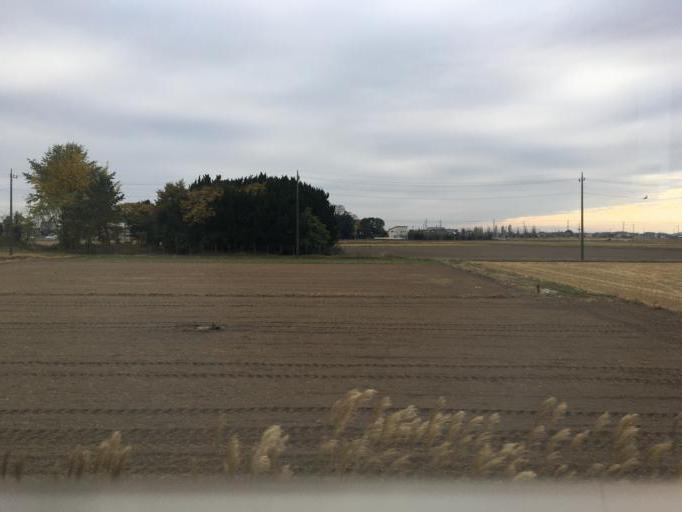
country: JP
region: Tochigi
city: Tochigi
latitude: 36.3534
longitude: 139.7763
